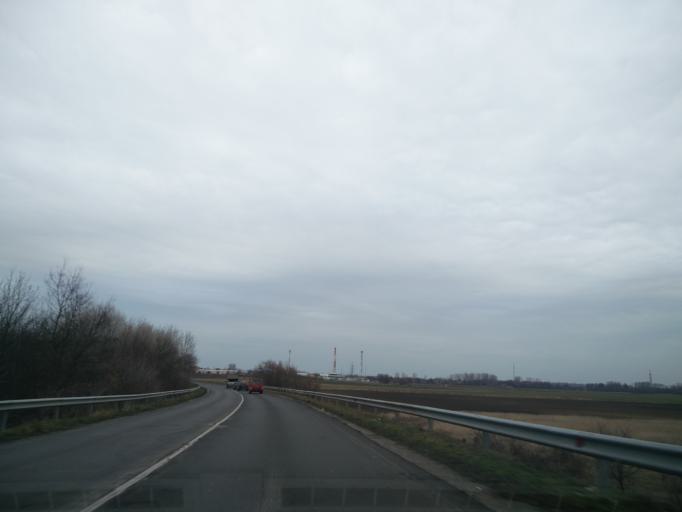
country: HU
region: Pest
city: Vecses
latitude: 47.3924
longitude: 19.3111
